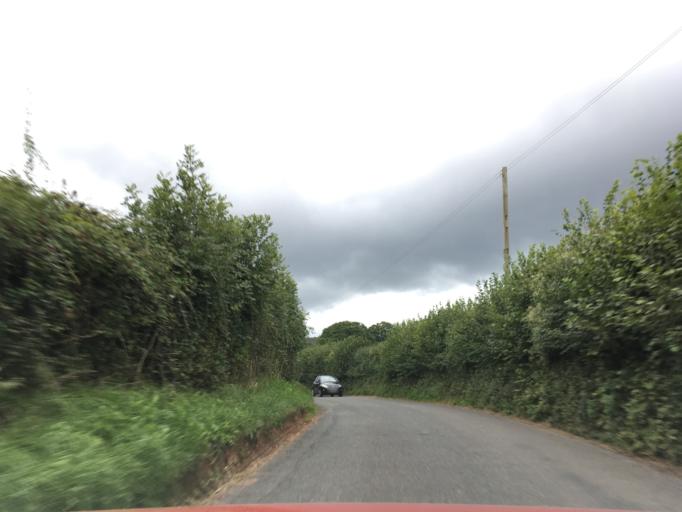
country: GB
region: Wales
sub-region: Newport
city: Llanvaches
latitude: 51.6255
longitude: -2.7933
